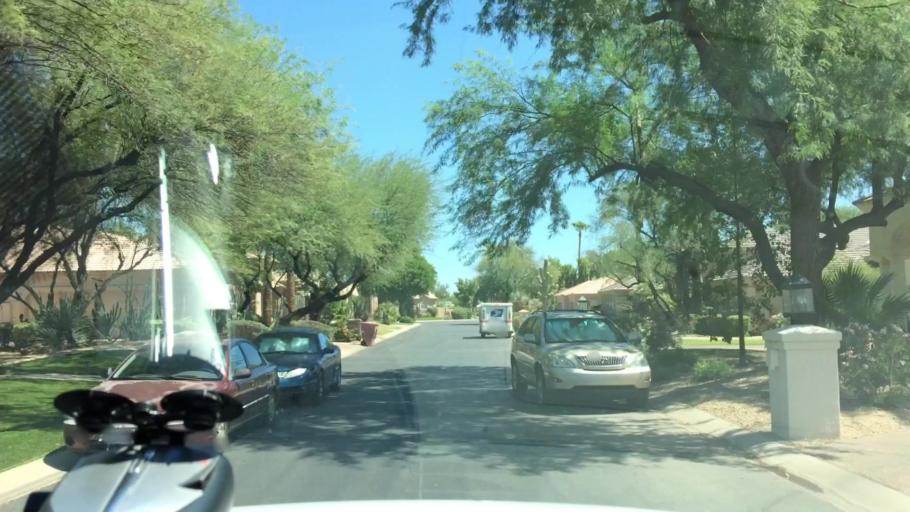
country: US
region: Arizona
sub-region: Maricopa County
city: Scottsdale
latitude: 33.5945
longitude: -111.8727
